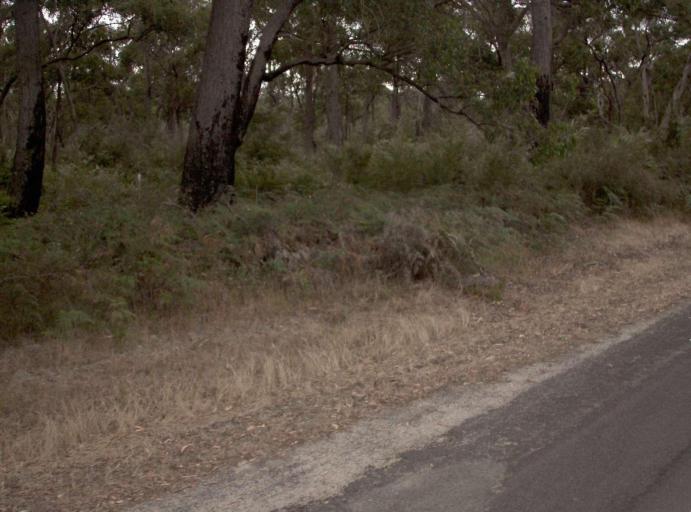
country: AU
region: Victoria
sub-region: Wellington
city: Sale
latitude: -38.4649
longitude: 146.9324
